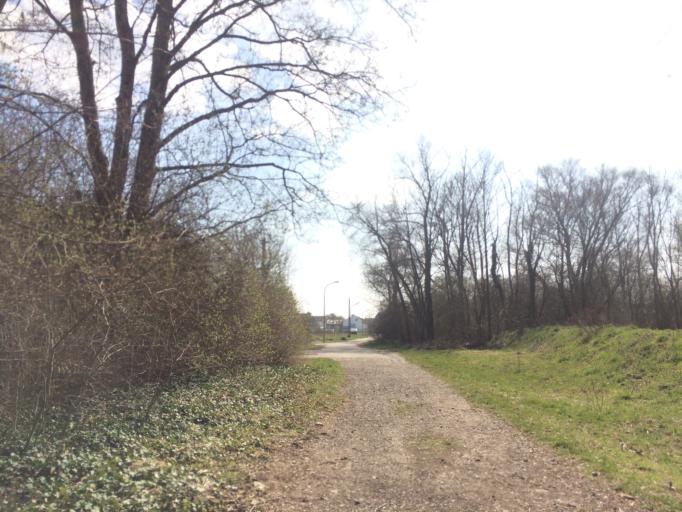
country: DE
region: Bavaria
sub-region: Swabia
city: Gersthofen
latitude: 48.4124
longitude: 10.8974
